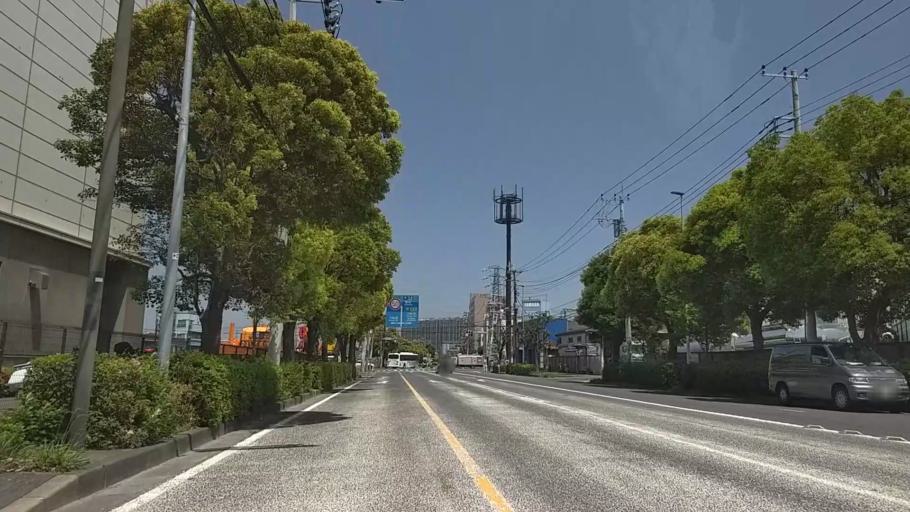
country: JP
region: Kanagawa
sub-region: Kawasaki-shi
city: Kawasaki
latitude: 35.5246
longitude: 139.7471
